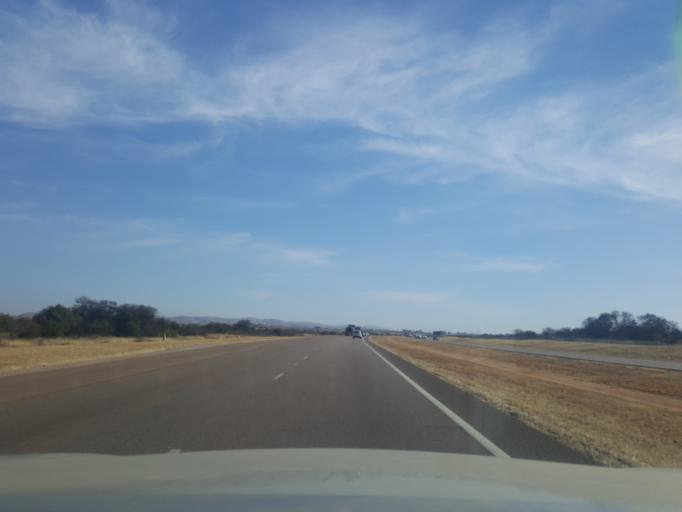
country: ZA
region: Gauteng
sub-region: City of Tshwane Metropolitan Municipality
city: Pretoria
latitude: -25.6447
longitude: 28.1692
